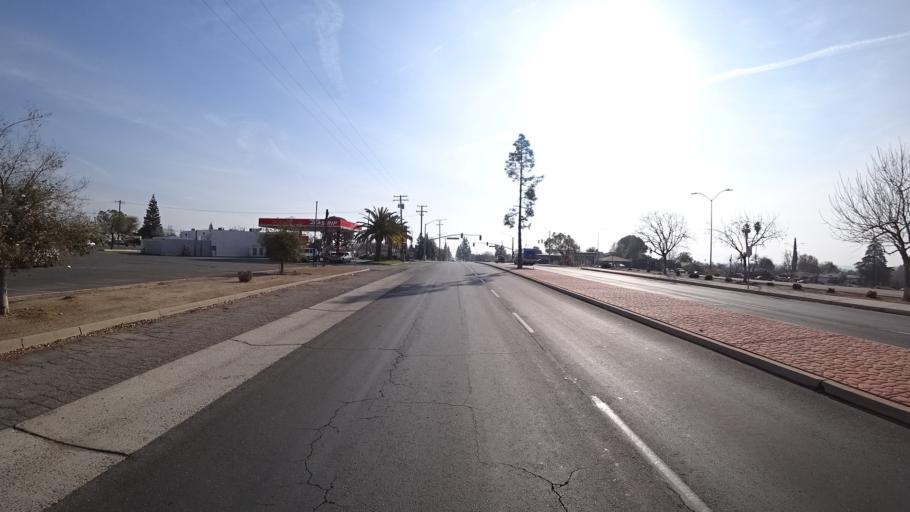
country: US
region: California
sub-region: Kern County
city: Oildale
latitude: 35.4059
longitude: -118.9675
